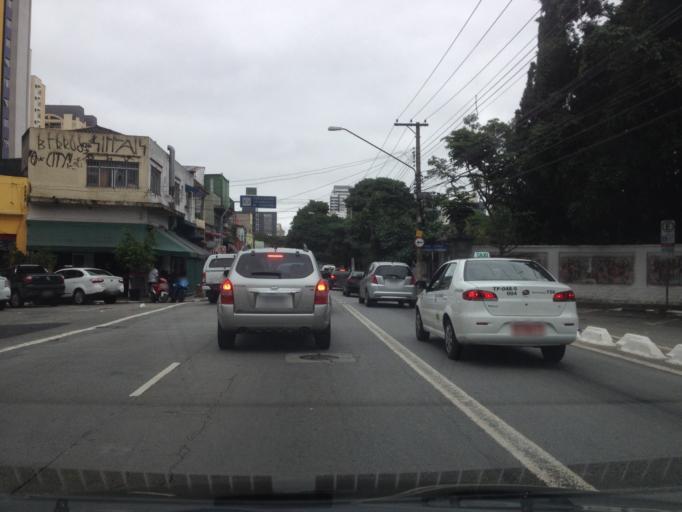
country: BR
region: Sao Paulo
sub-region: Sao Paulo
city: Sao Paulo
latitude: -23.5590
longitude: -46.6840
